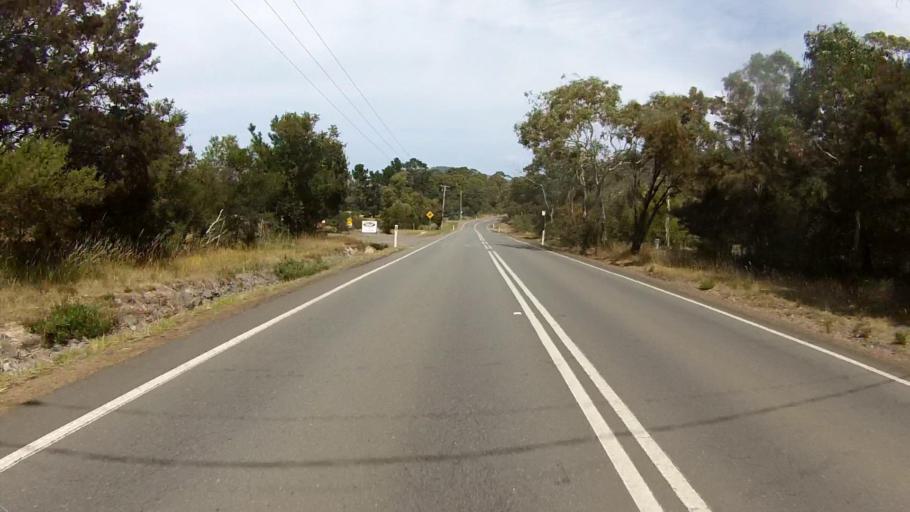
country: AU
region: Tasmania
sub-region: Clarence
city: Sandford
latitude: -43.0121
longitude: 147.4916
